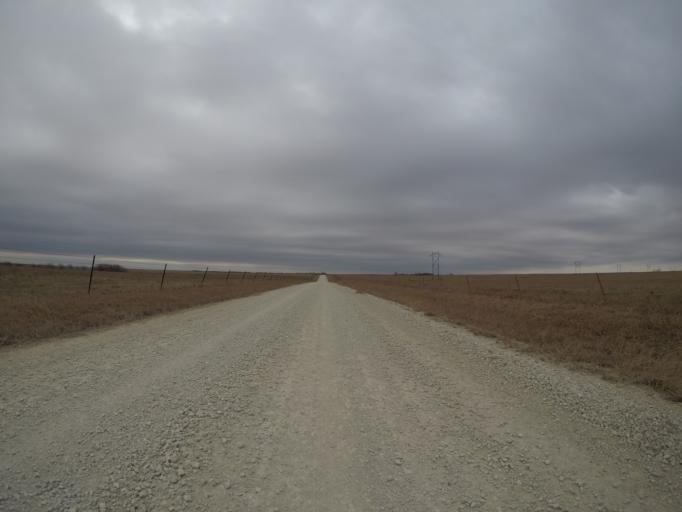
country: US
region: Kansas
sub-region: Wabaunsee County
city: Alma
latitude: 38.7555
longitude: -96.1496
